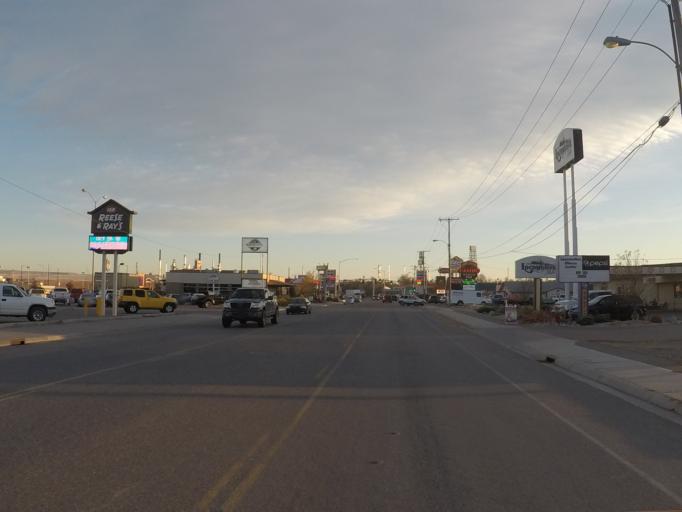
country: US
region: Montana
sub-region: Yellowstone County
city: Laurel
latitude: 45.6670
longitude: -108.7715
